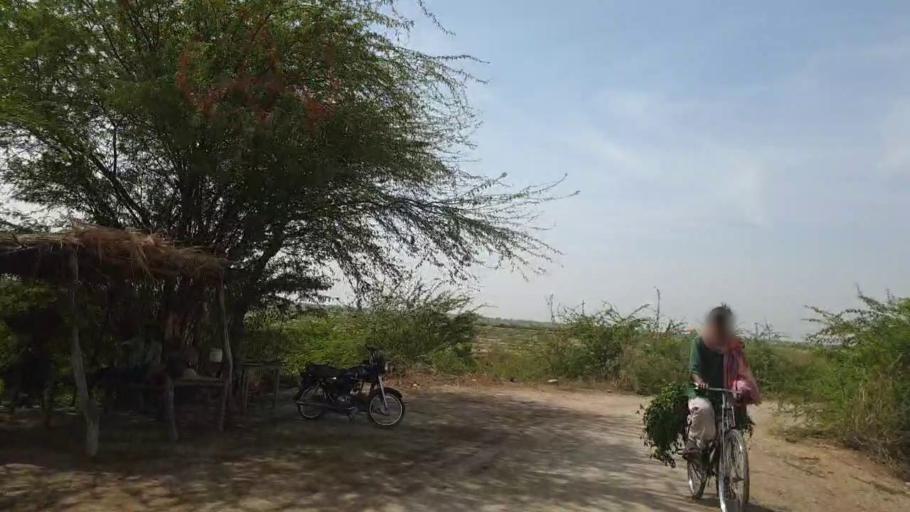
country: PK
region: Sindh
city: Kunri
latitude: 25.1943
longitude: 69.5631
